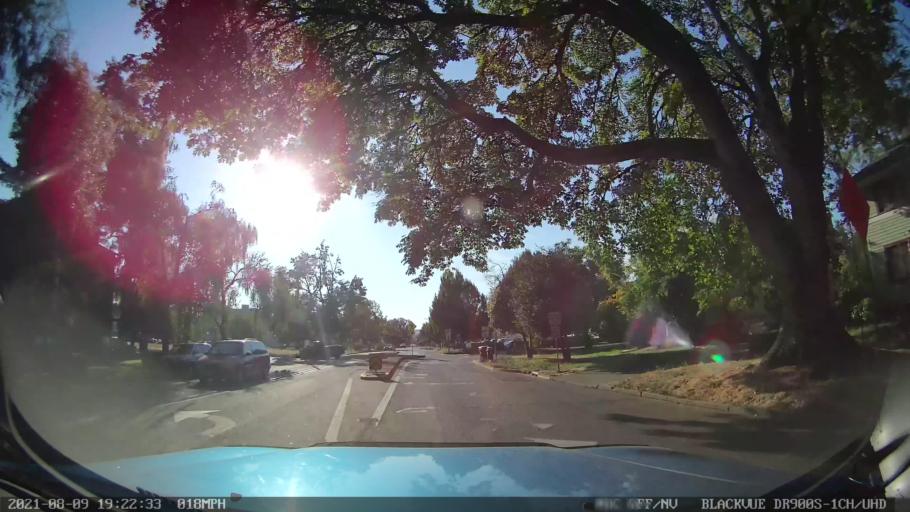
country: US
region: Oregon
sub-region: Marion County
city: Salem
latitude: 44.9398
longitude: -123.0235
